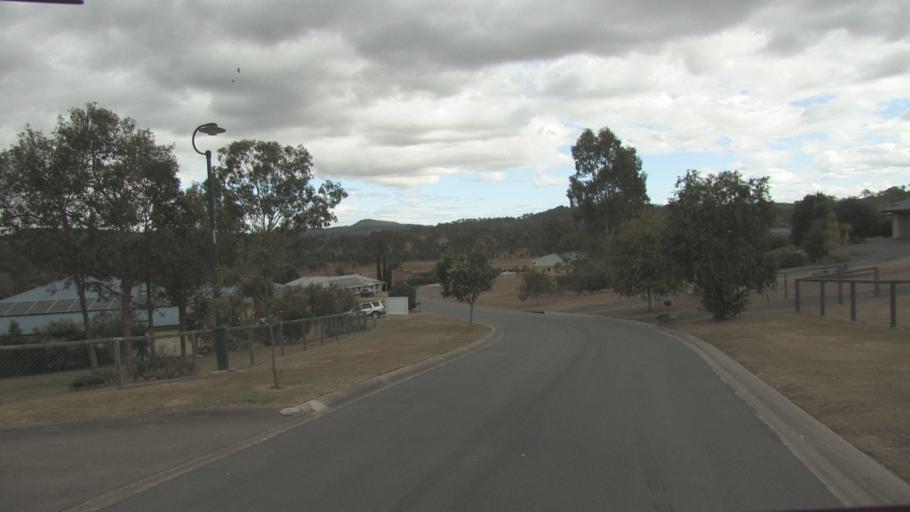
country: AU
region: Queensland
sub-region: Logan
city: Cedar Vale
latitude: -27.8778
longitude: 153.0758
